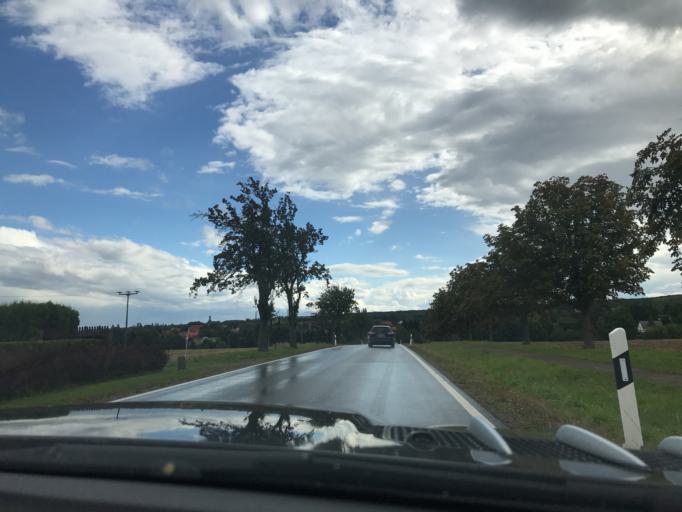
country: DE
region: Thuringia
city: Mulverstedt
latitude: 51.1145
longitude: 10.5072
